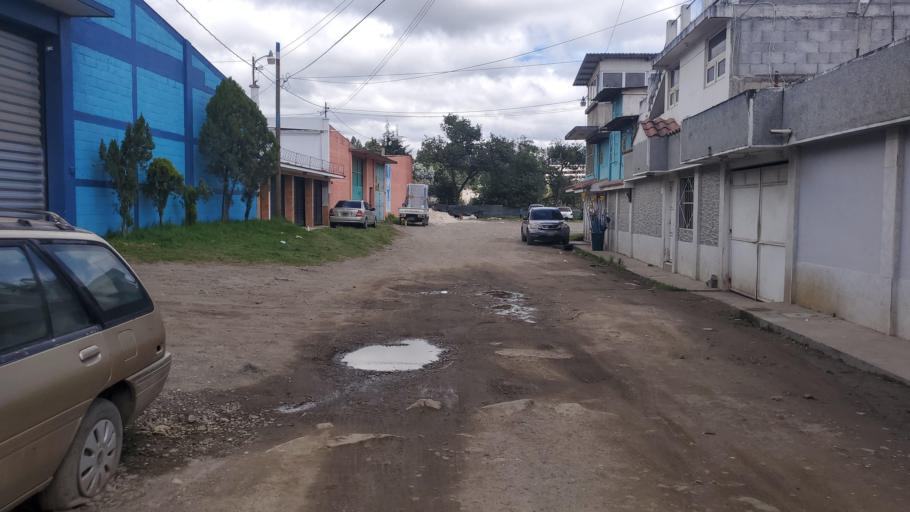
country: GT
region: Quetzaltenango
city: Quetzaltenango
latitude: 14.8380
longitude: -91.5387
